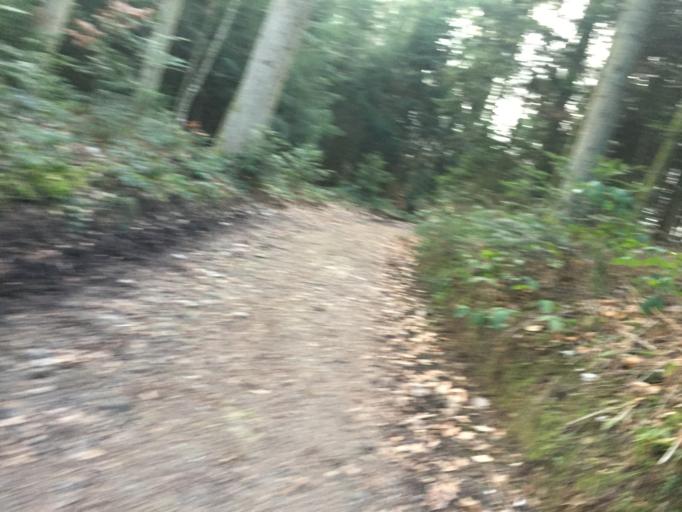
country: CH
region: Bern
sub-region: Bern-Mittelland District
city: Taegertschi
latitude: 46.8865
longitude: 7.5769
